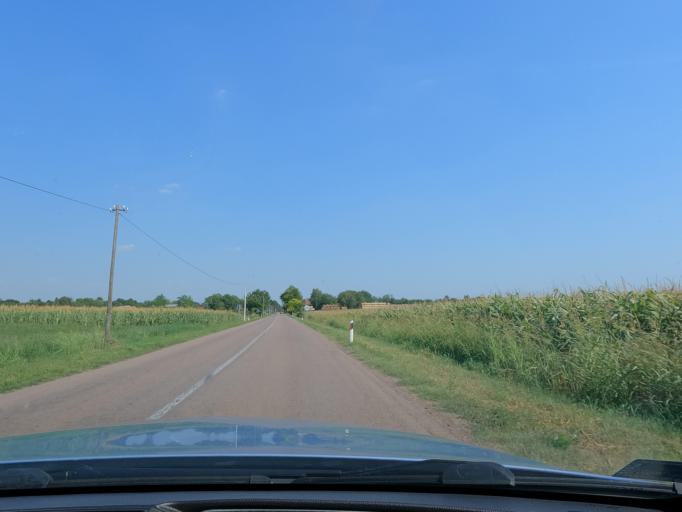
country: RS
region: Autonomna Pokrajina Vojvodina
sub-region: Severnobacki Okrug
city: Mali Igos
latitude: 45.7649
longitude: 19.7431
